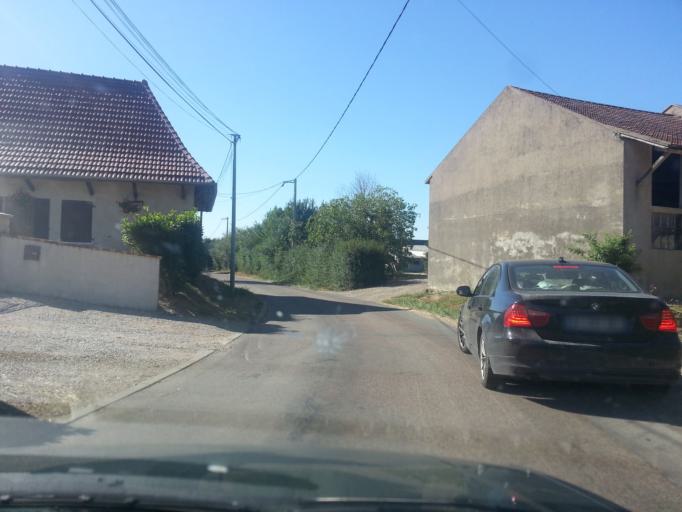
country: FR
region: Bourgogne
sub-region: Departement de Saone-et-Loire
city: Saint-Martin-en-Bresse
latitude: 46.7960
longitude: 5.0744
